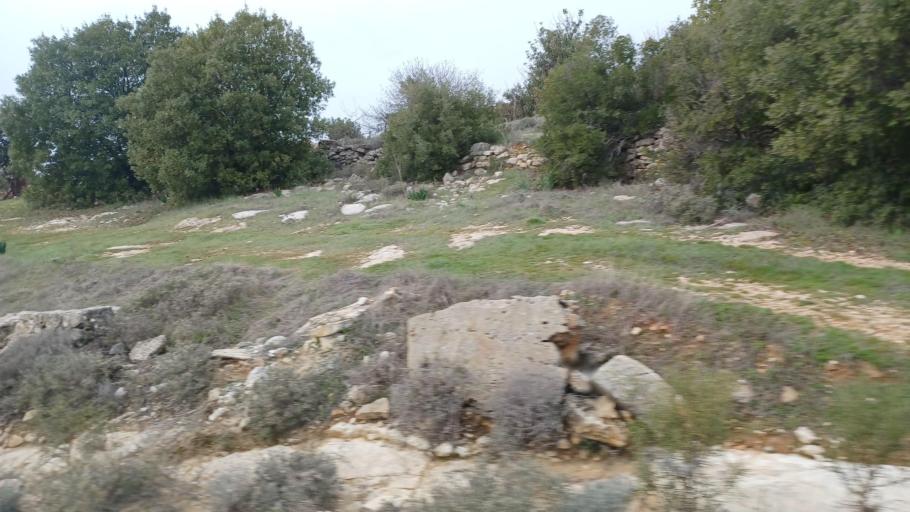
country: CY
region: Limassol
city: Pachna
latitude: 34.7656
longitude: 32.7574
